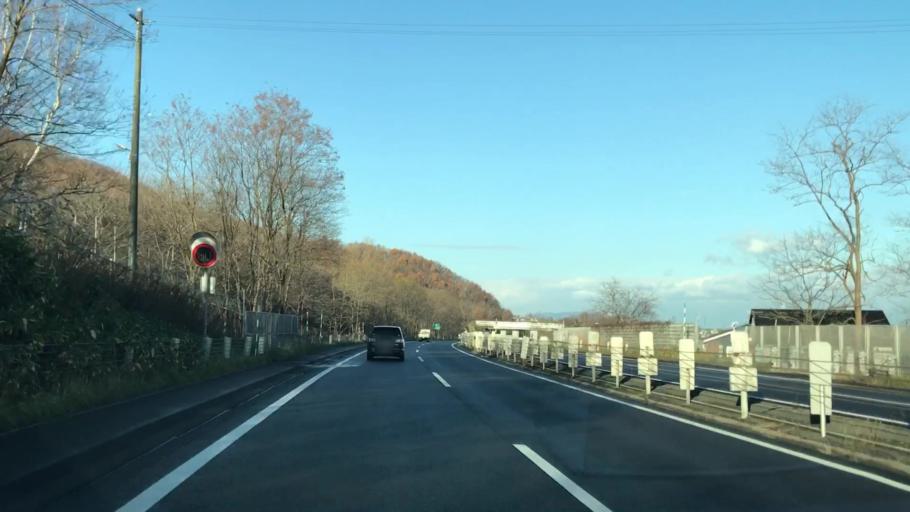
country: JP
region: Hokkaido
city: Sapporo
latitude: 43.1192
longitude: 141.2229
